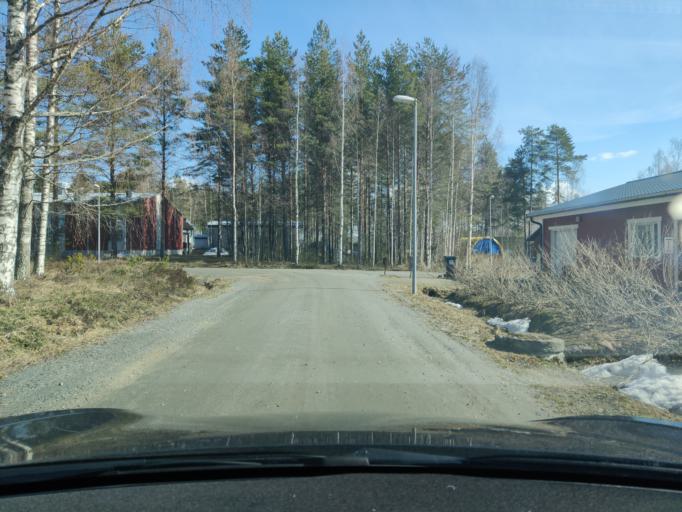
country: FI
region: Northern Savo
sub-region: Kuopio
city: Vehmersalmi
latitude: 62.7586
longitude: 28.0367
